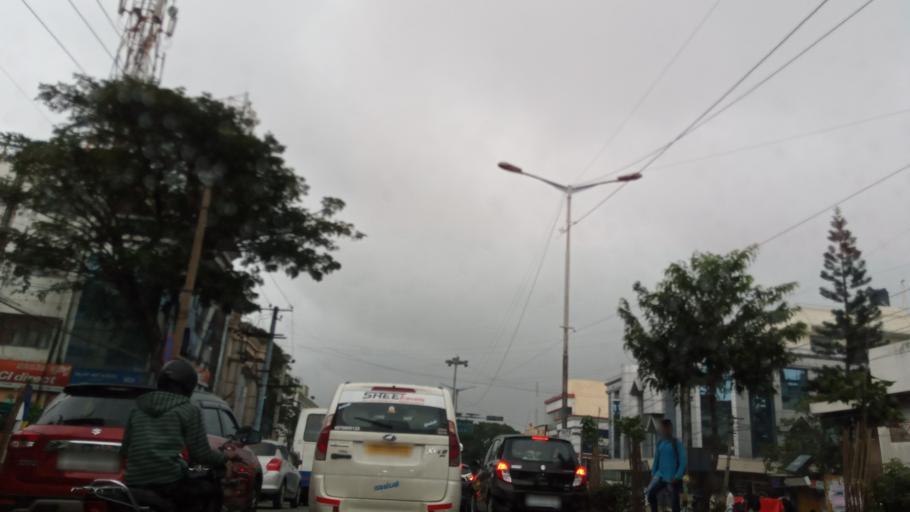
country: IN
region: Karnataka
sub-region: Bangalore Urban
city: Bangalore
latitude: 12.9258
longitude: 77.5492
